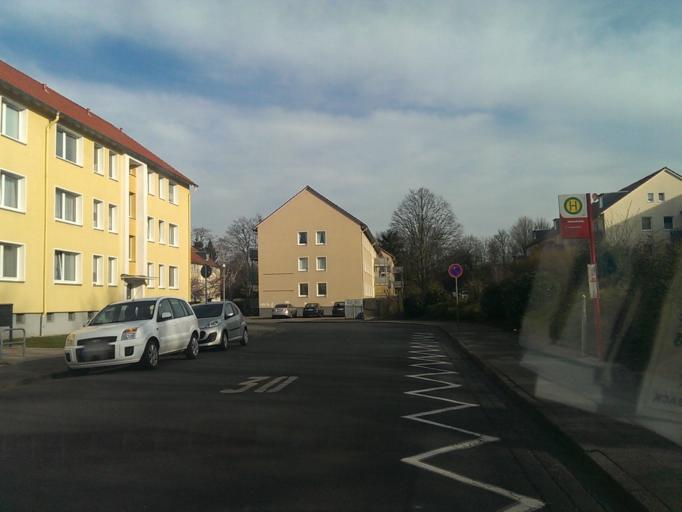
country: DE
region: Lower Saxony
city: Hildesheim
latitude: 52.1616
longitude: 9.9671
